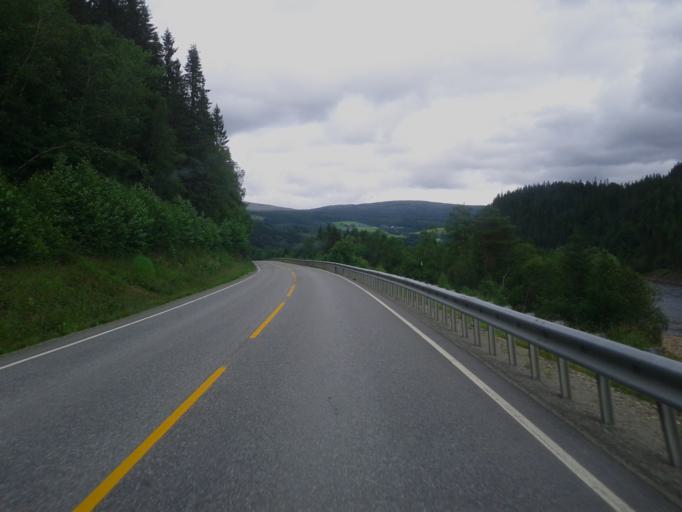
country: NO
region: Sor-Trondelag
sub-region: Midtre Gauldal
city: Storen
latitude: 62.9443
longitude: 10.6766
